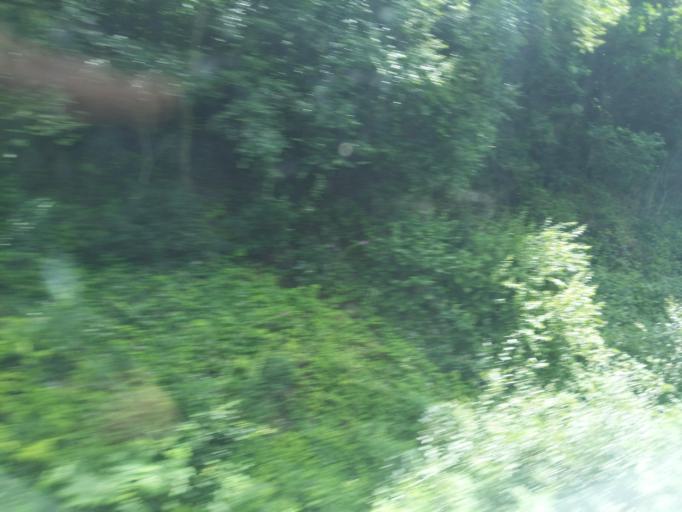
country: GB
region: England
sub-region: Cornwall
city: Lostwithiel
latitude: 50.3894
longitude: -4.6668
